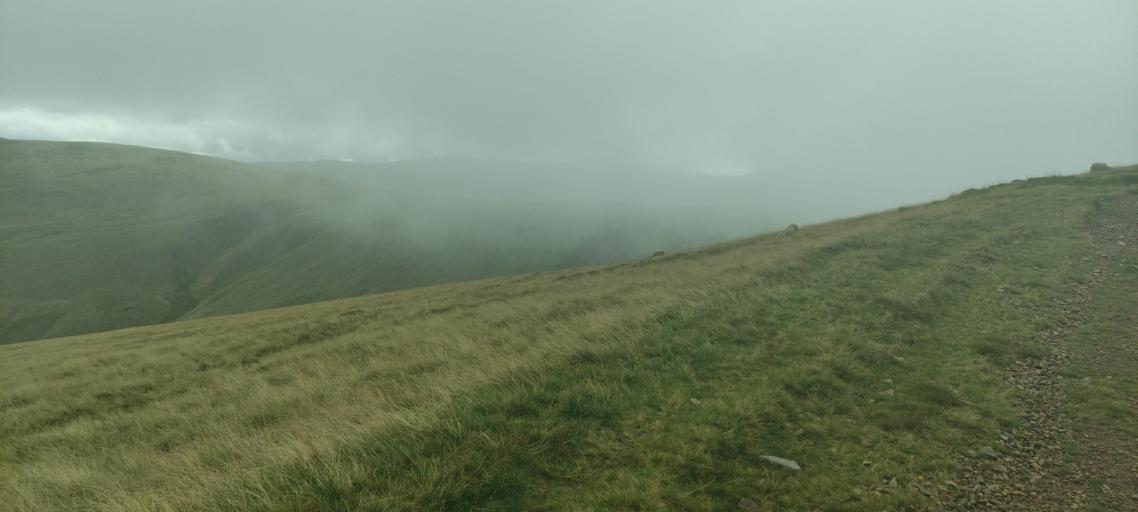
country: GB
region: England
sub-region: Cumbria
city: Keswick
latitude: 54.7040
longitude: -3.0551
